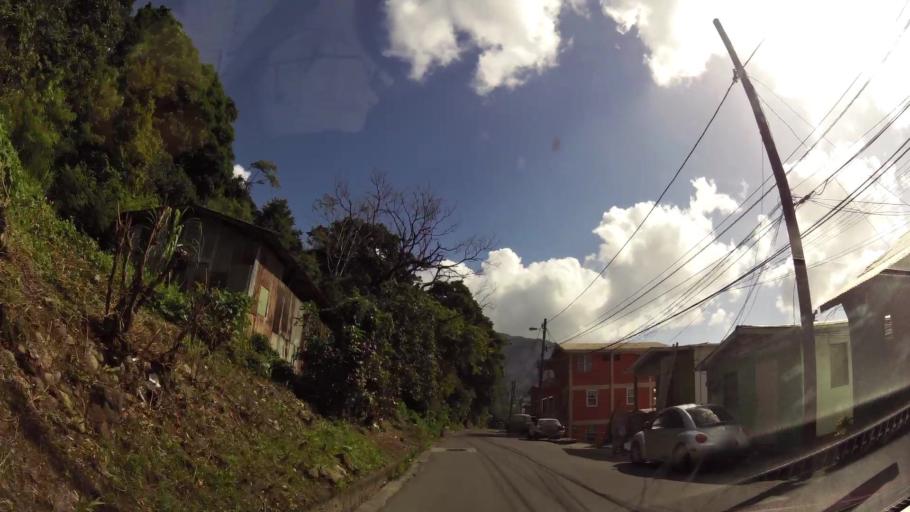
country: DM
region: Saint George
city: Roseau
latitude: 15.2883
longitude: -61.3764
